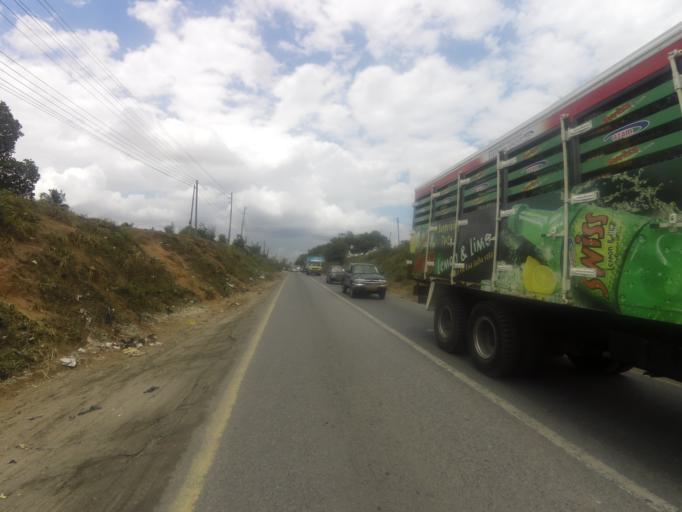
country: TZ
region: Pwani
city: Vikindu
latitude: -6.9442
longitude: 39.2795
